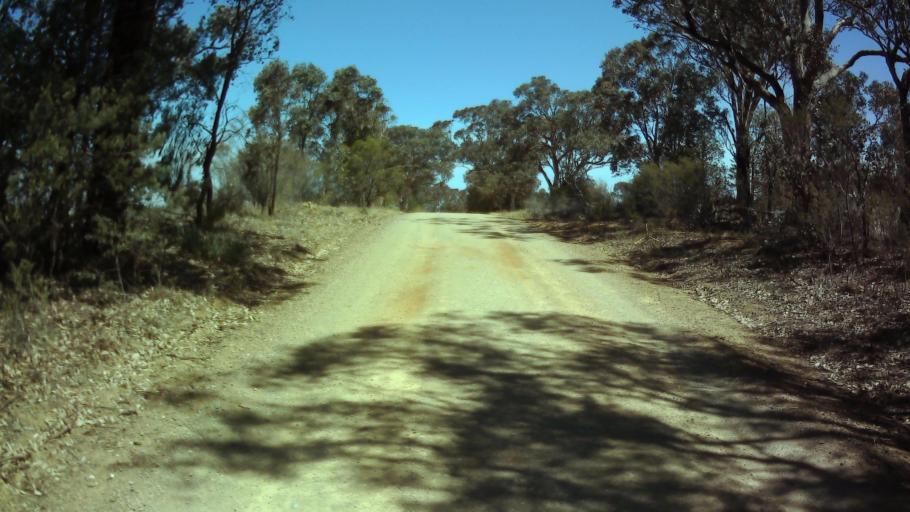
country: AU
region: New South Wales
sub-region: Weddin
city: Grenfell
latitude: -33.9148
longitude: 148.1786
